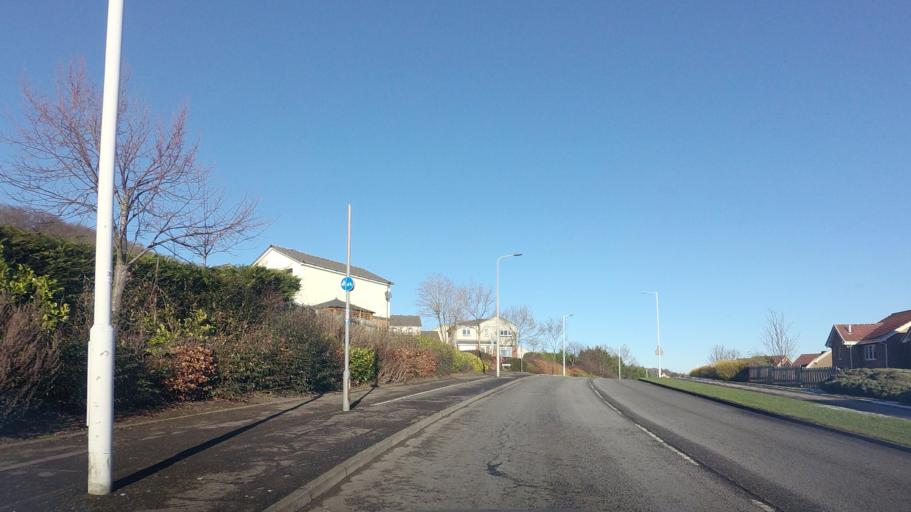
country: GB
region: Scotland
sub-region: Fife
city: Inverkeithing
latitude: 56.0341
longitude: -3.3702
